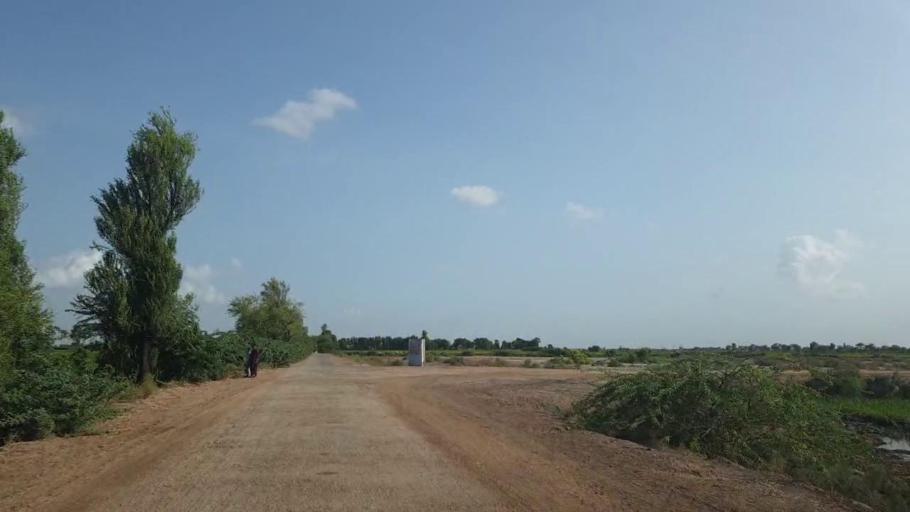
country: PK
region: Sindh
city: Kadhan
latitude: 24.6269
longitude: 69.0959
